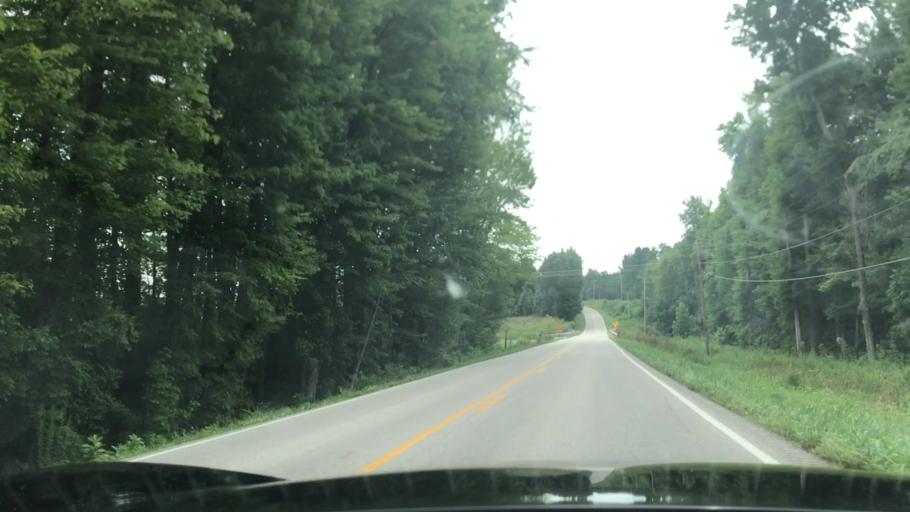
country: US
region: Kentucky
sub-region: Ohio County
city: Oak Grove
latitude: 37.1955
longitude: -86.8843
